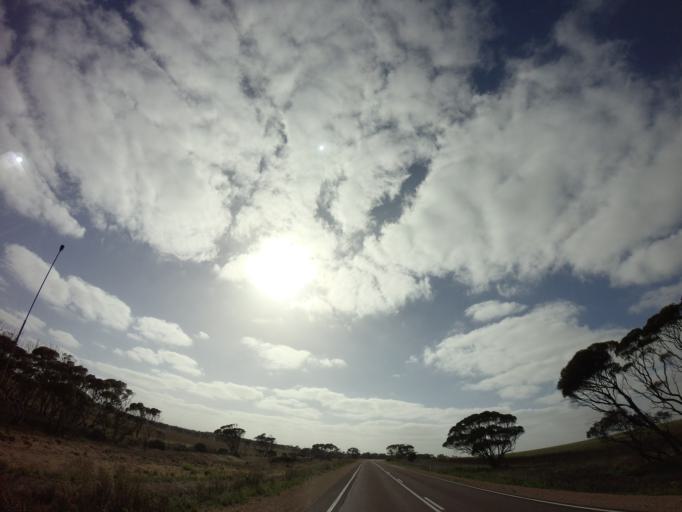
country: AU
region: South Australia
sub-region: Streaky Bay
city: Streaky Bay
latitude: -32.2822
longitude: 134.2245
